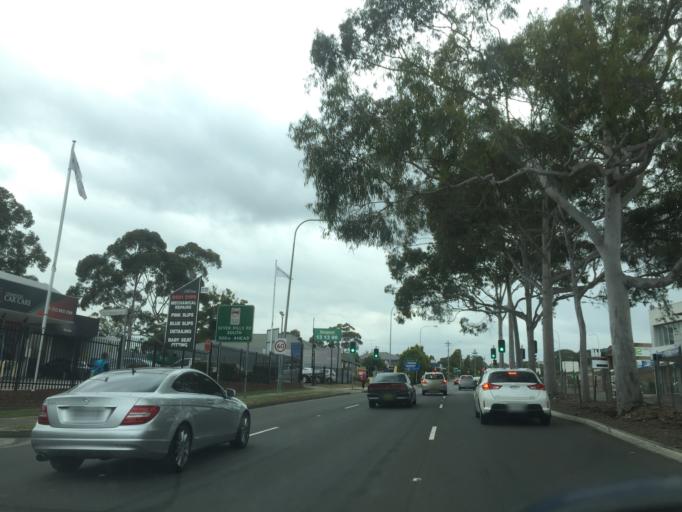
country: AU
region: New South Wales
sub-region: Blacktown
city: Blacktown
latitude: -33.7755
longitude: 150.9343
